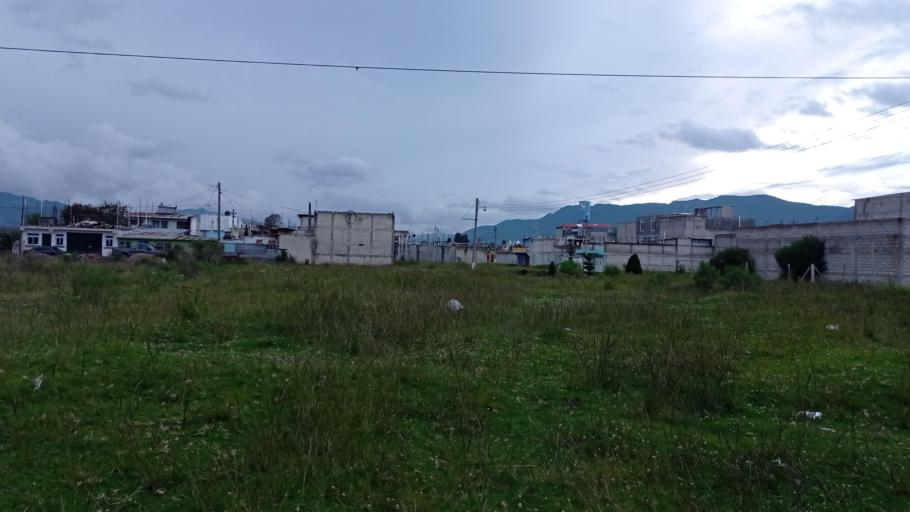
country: GT
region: Quetzaltenango
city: Olintepeque
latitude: 14.8641
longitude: -91.5077
